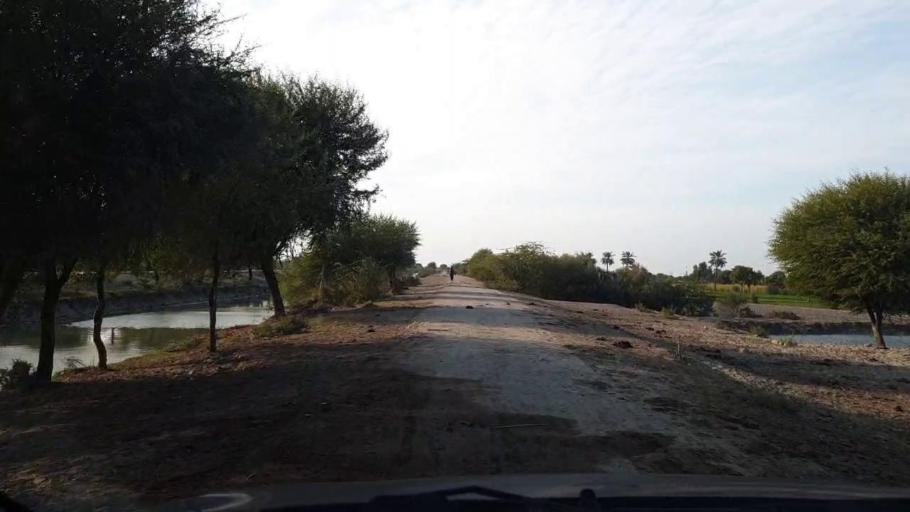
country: PK
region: Sindh
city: Jhol
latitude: 25.9499
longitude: 68.8589
